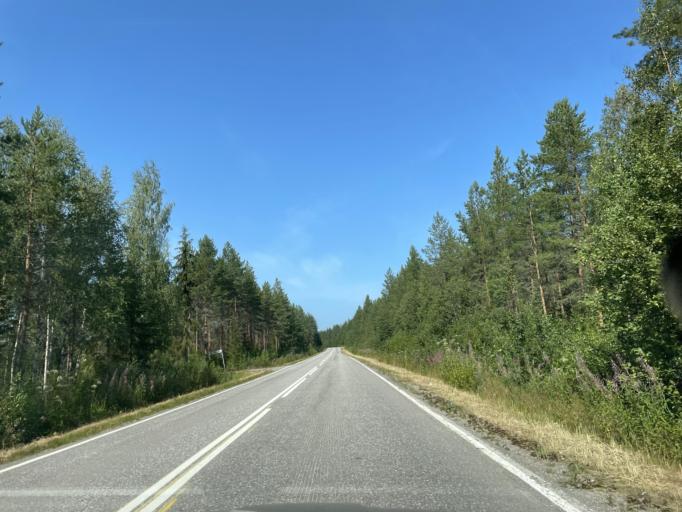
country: FI
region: Central Finland
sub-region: Saarijaervi-Viitasaari
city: Pihtipudas
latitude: 63.3630
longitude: 25.7189
